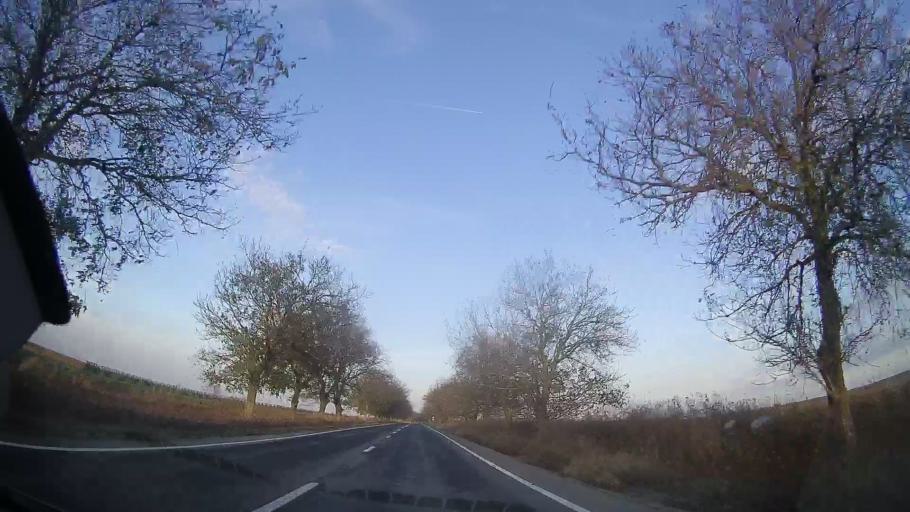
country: RO
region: Constanta
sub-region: Comuna Comana
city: Comana
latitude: 43.8723
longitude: 28.2766
